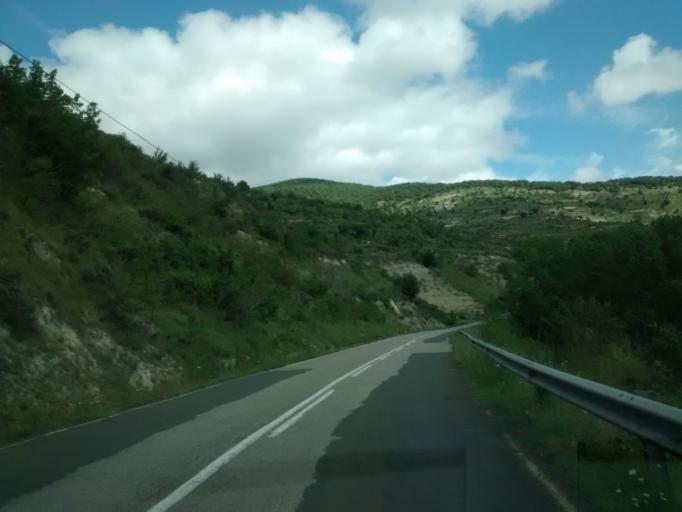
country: ES
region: La Rioja
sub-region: Provincia de La Rioja
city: Terroba
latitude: 42.2511
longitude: -2.4550
